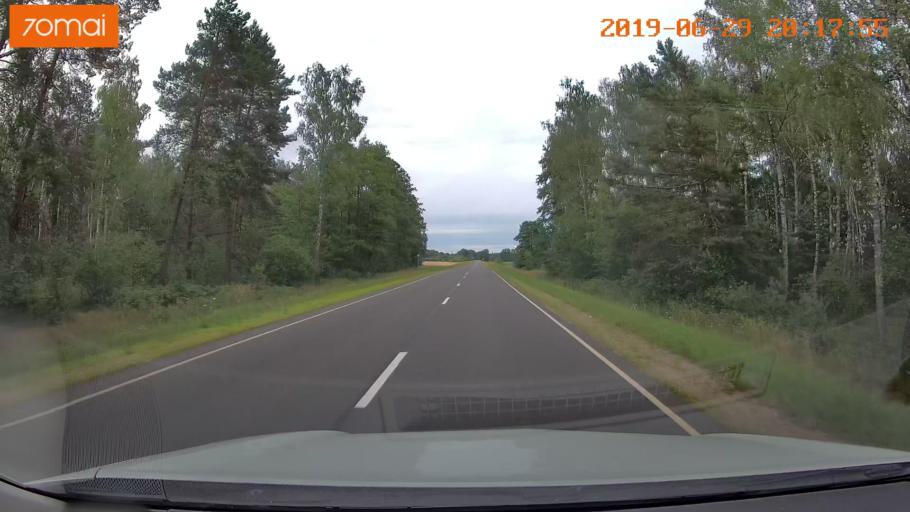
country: BY
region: Brest
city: Asnyezhytsy
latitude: 52.3914
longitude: 26.2261
